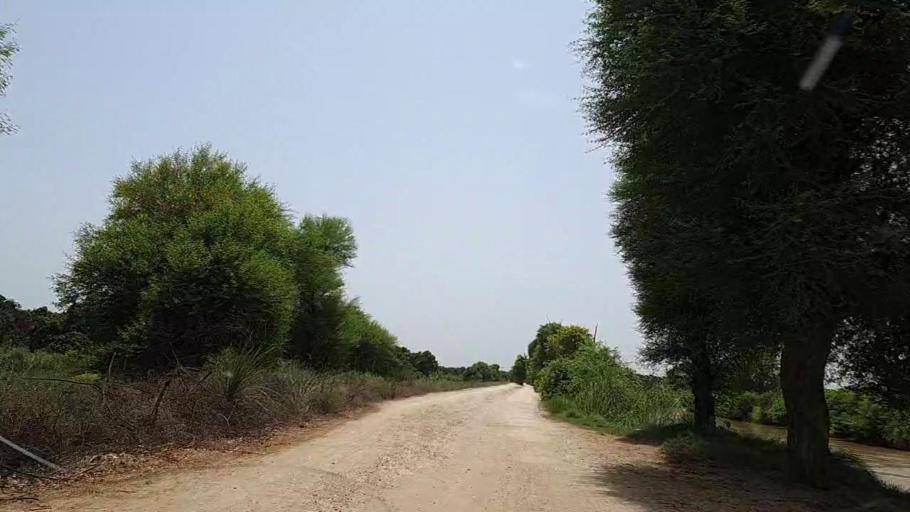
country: PK
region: Sindh
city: Tharu Shah
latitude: 27.0032
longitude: 68.1215
